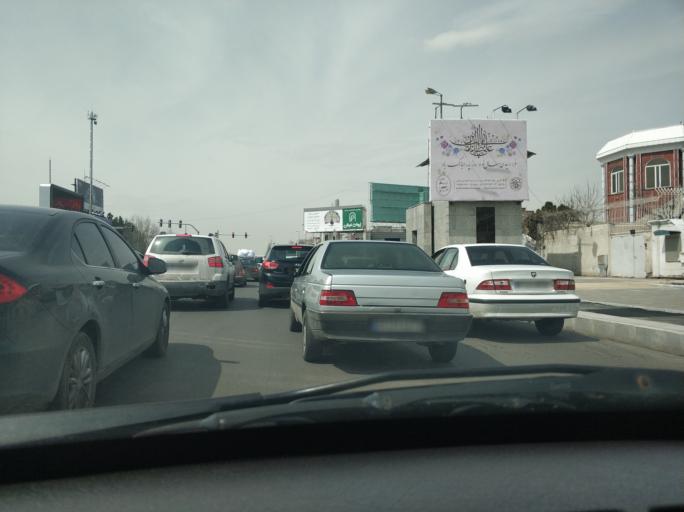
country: IR
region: Razavi Khorasan
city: Mashhad
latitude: 36.3069
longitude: 59.5532
